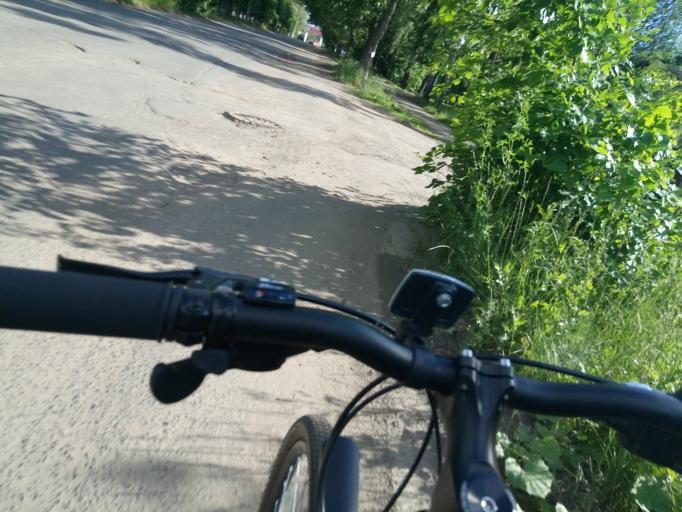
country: RU
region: Jaroslavl
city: Yaroslavl
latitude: 57.6398
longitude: 39.9122
